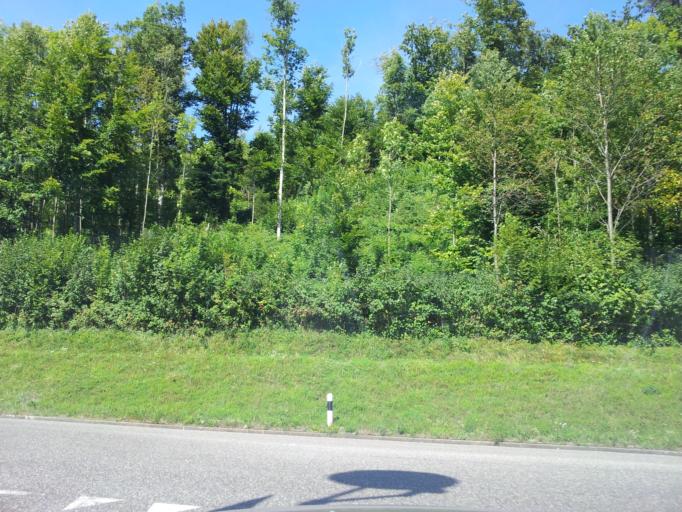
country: CH
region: Saint Gallen
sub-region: Wahlkreis See-Gaster
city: Jona
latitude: 47.2295
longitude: 8.8588
